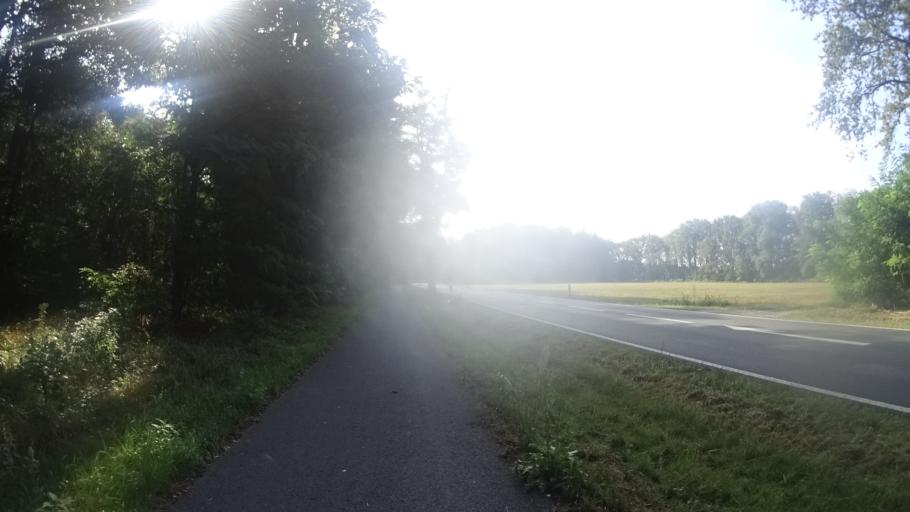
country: DE
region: Brandenburg
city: Cumlosen
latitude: 53.0178
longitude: 11.7029
